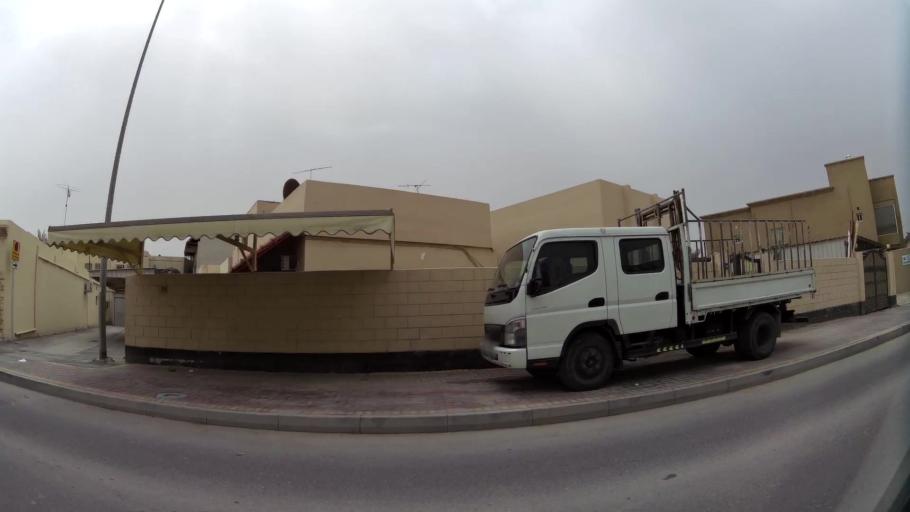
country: BH
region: Northern
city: Madinat `Isa
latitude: 26.1859
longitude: 50.5393
